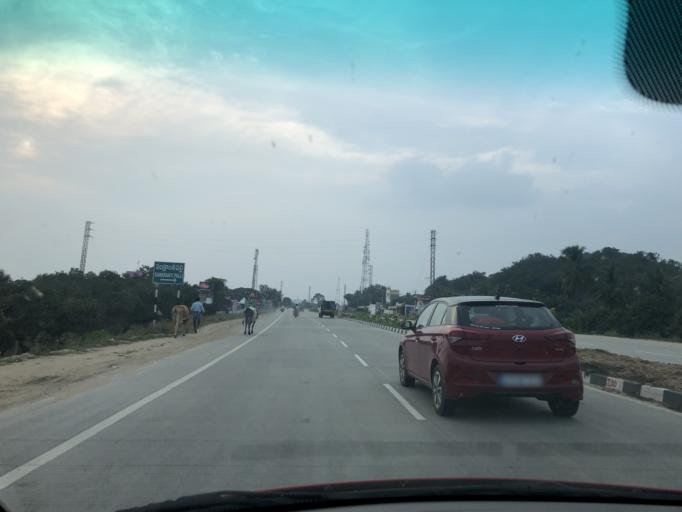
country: IN
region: Andhra Pradesh
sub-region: Chittoor
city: Chittoor
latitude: 13.1957
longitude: 79.0074
